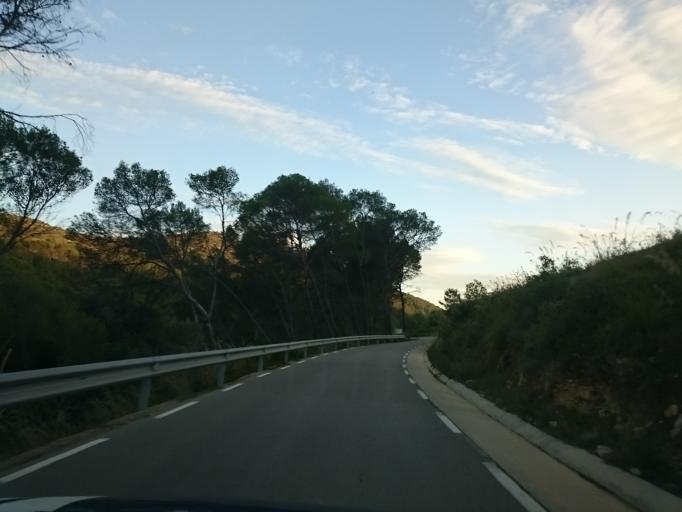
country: ES
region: Catalonia
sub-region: Provincia de Barcelona
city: Olivella
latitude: 41.3107
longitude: 1.7848
